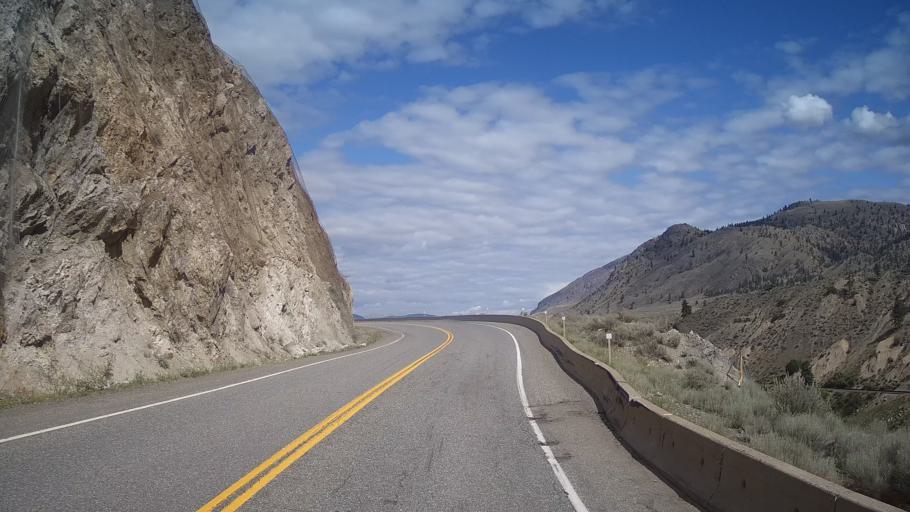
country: CA
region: British Columbia
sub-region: Thompson-Nicola Regional District
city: Ashcroft
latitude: 50.5372
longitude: -121.2867
